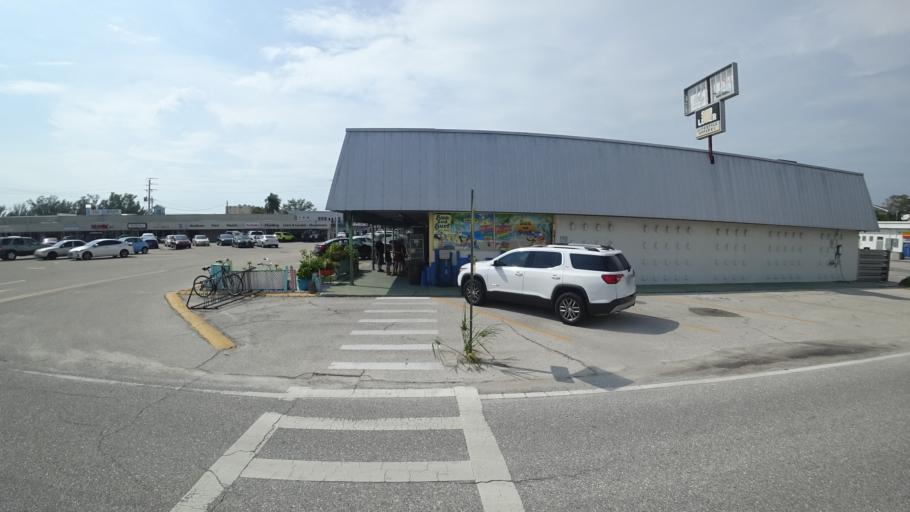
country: US
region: Florida
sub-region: Manatee County
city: Holmes Beach
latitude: 27.5069
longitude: -82.7143
